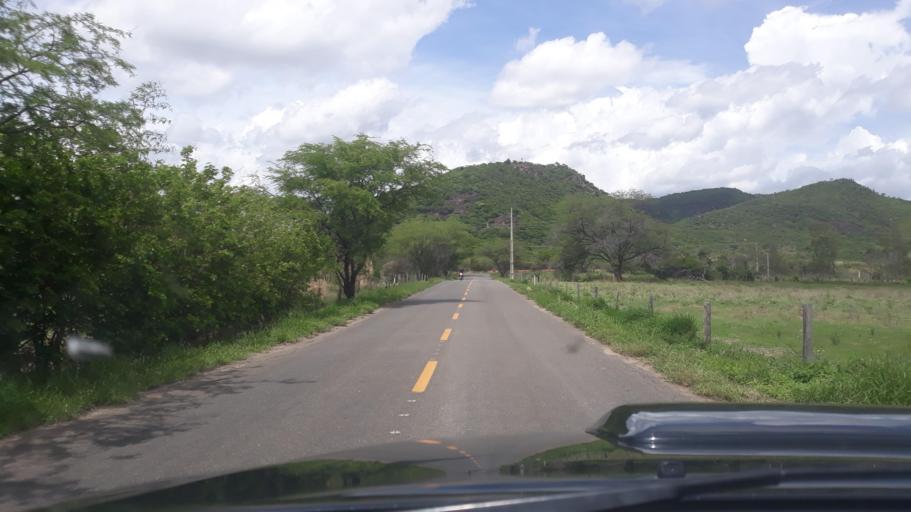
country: BR
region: Bahia
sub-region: Guanambi
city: Guanambi
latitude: -14.2742
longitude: -42.7108
